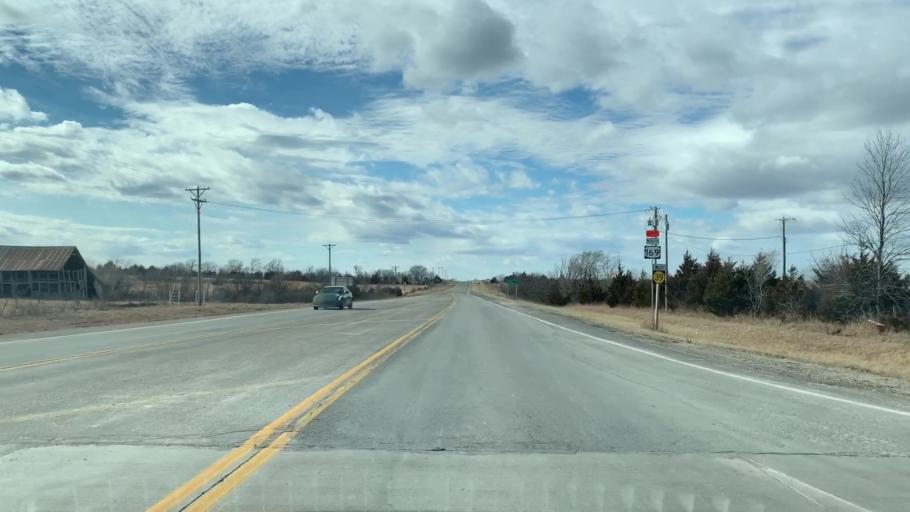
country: US
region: Kansas
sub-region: Neosho County
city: Chanute
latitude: 37.6892
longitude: -95.4807
